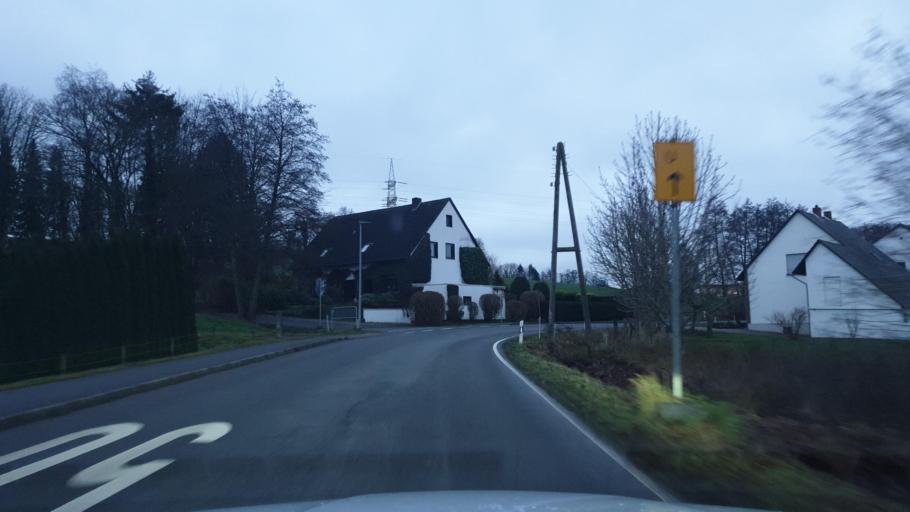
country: DE
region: North Rhine-Westphalia
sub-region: Regierungsbezirk Detmold
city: Vlotho
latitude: 52.1705
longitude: 8.8270
